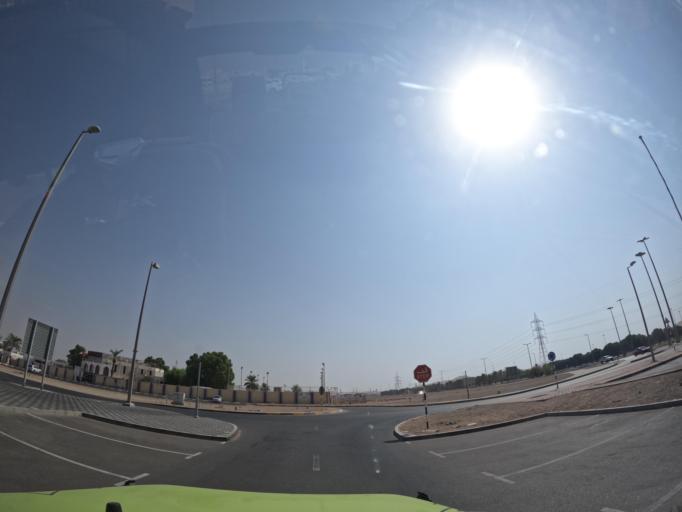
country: AE
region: Abu Dhabi
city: Al Ain
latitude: 24.2249
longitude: 55.5528
